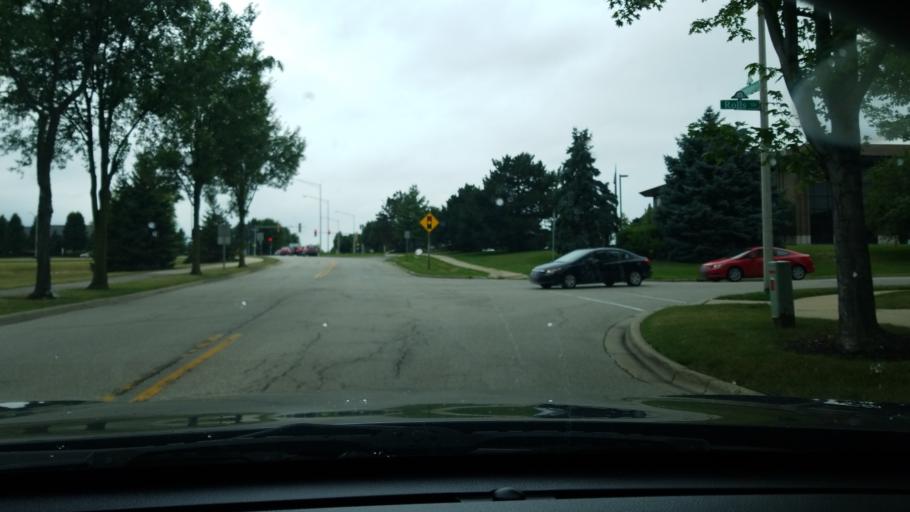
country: US
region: Illinois
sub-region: McHenry County
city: Lake in the Hills
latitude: 42.1685
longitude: -88.3332
